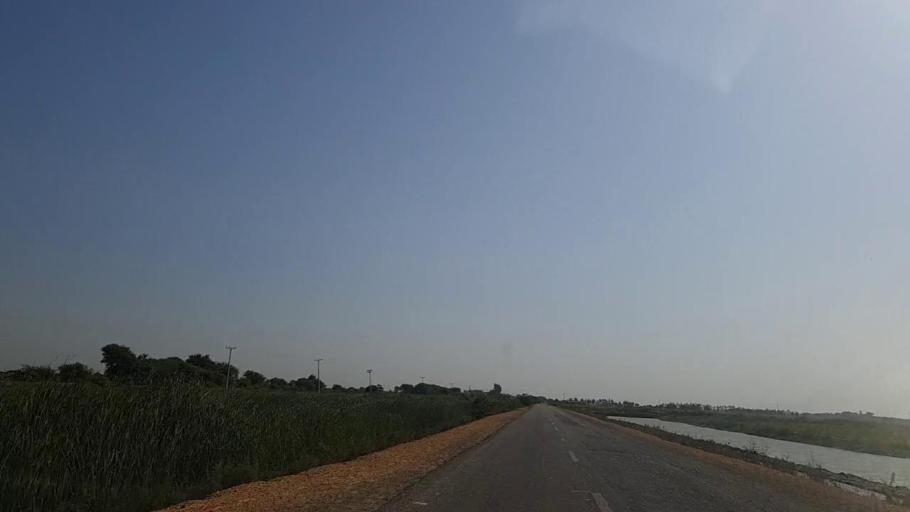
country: PK
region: Sindh
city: Jati
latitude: 24.4983
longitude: 68.2748
